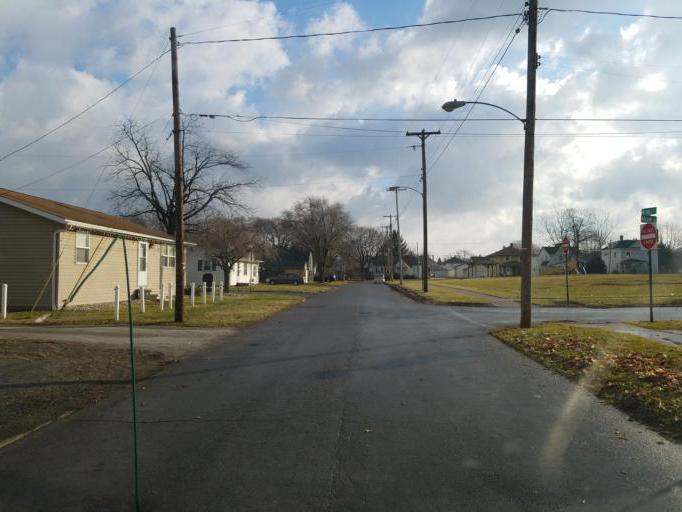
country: US
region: Ohio
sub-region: Marion County
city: Marion
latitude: 40.5791
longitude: -83.1393
